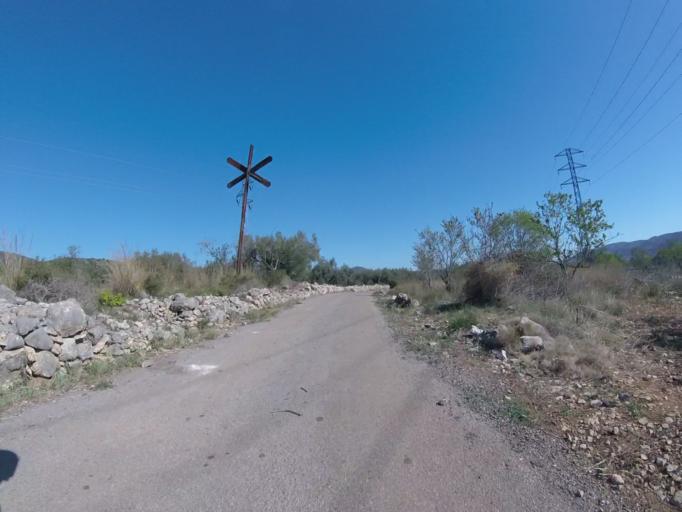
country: ES
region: Valencia
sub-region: Provincia de Castello
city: Santa Magdalena de Pulpis
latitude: 40.3503
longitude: 0.2781
